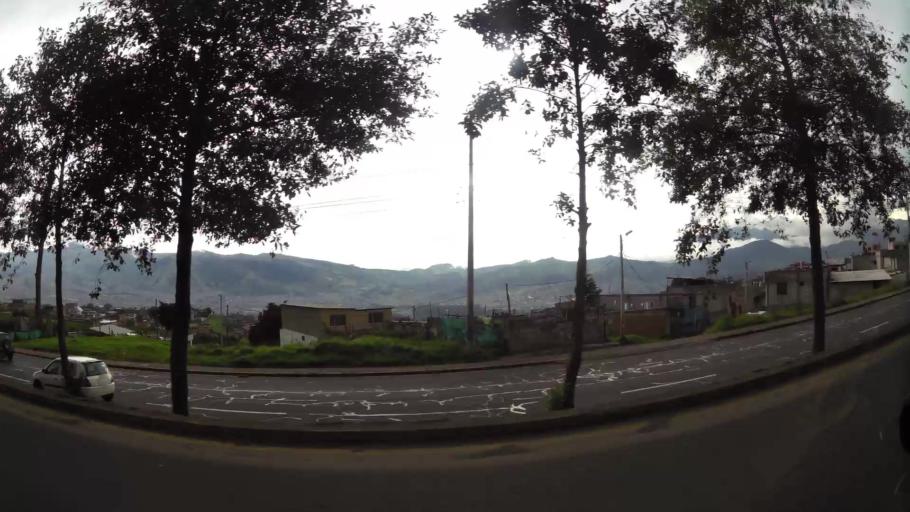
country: EC
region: Pichincha
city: Quito
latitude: -0.2952
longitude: -78.5201
